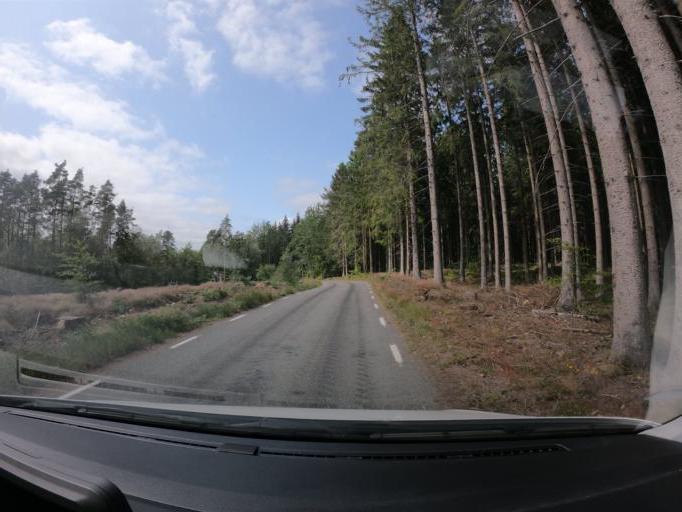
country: SE
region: Skane
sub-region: Hassleholms Kommun
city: Sosdala
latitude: 56.1176
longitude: 13.6160
